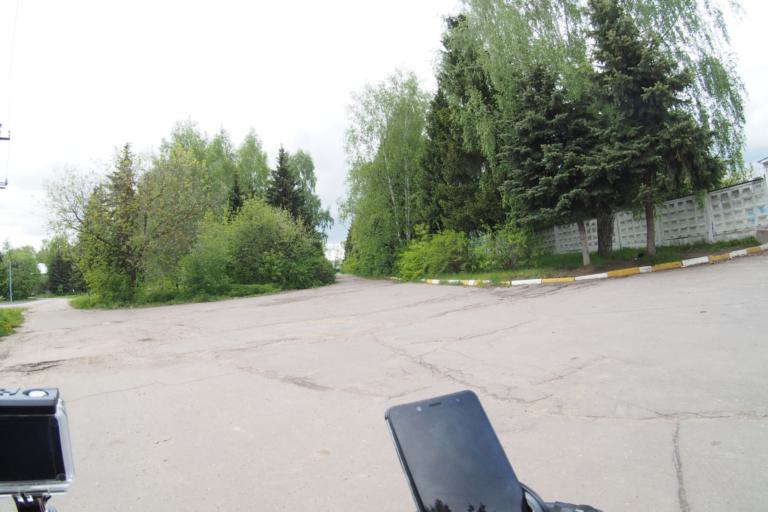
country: RU
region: Moskovskaya
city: Rechitsy
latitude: 55.5849
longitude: 38.5059
